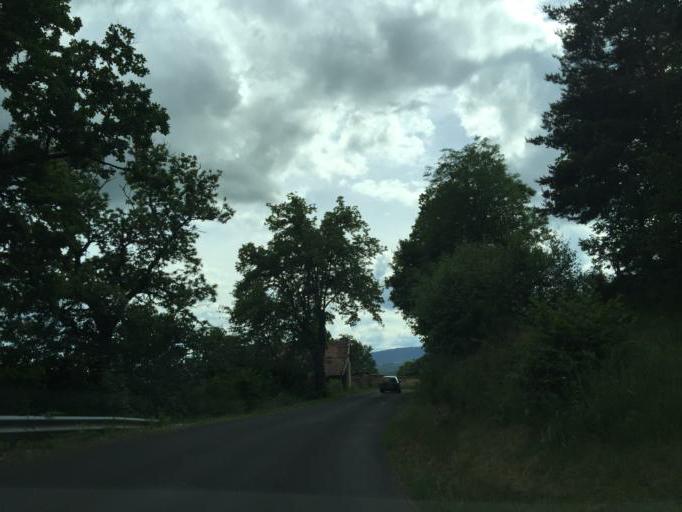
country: FR
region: Auvergne
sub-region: Departement du Puy-de-Dome
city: Ambert
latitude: 45.5446
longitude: 3.7731
